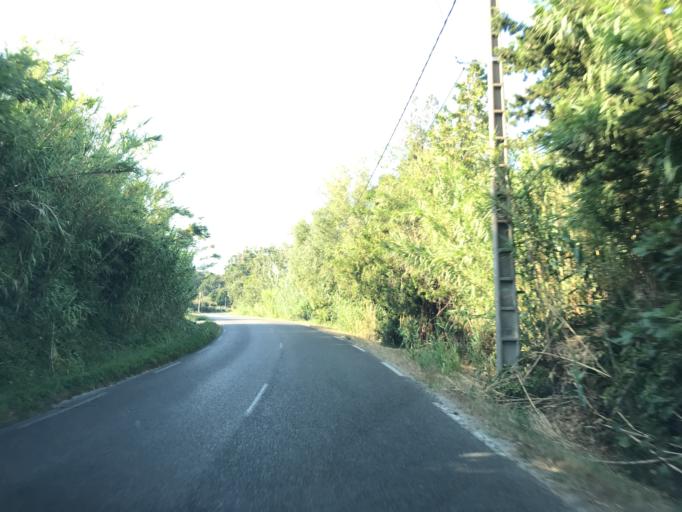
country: FR
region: Provence-Alpes-Cote d'Azur
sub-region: Departement des Bouches-du-Rhone
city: Saint-Chamas
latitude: 43.5633
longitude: 5.0158
